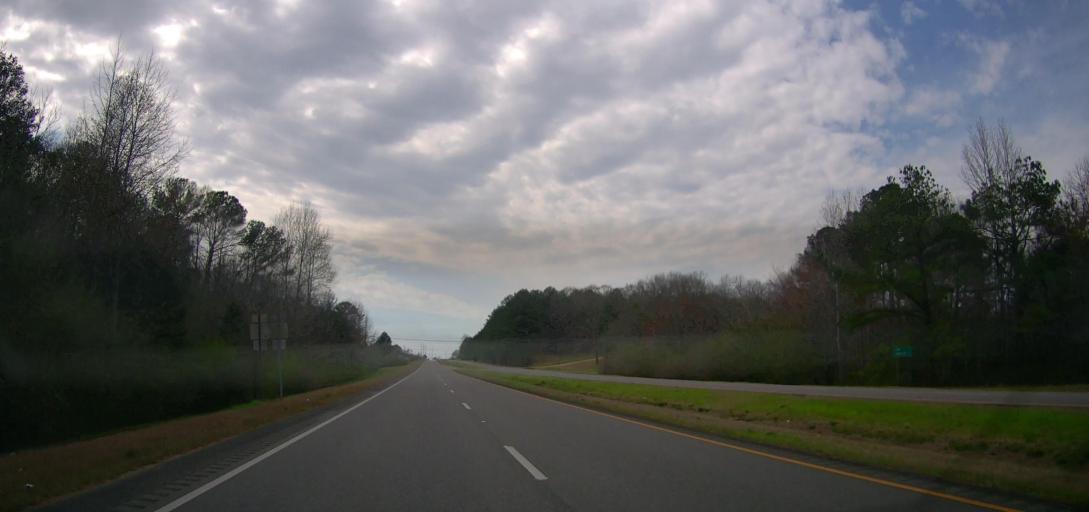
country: US
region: Alabama
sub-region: Marion County
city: Winfield
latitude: 33.9287
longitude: -87.7625
